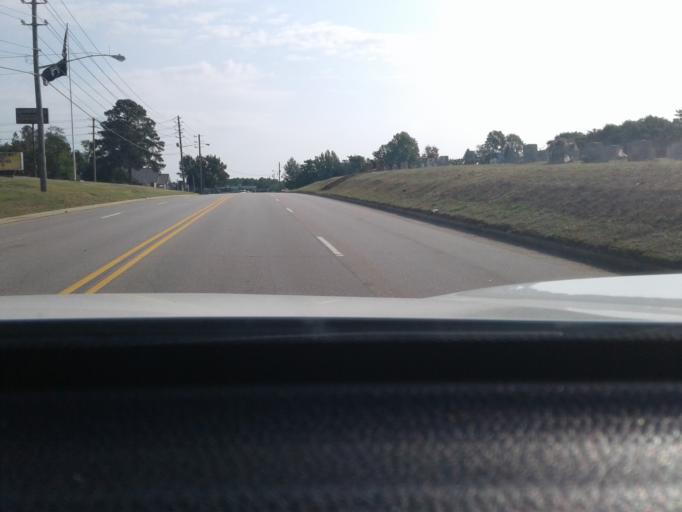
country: US
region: North Carolina
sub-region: Johnston County
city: Benson
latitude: 35.3861
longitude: -78.5454
